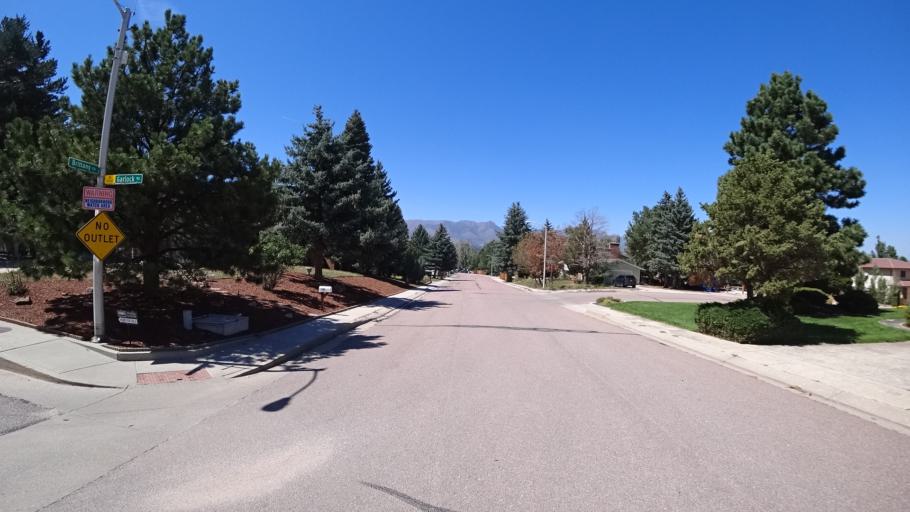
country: US
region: Colorado
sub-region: El Paso County
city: Colorado Springs
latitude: 38.9235
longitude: -104.8050
